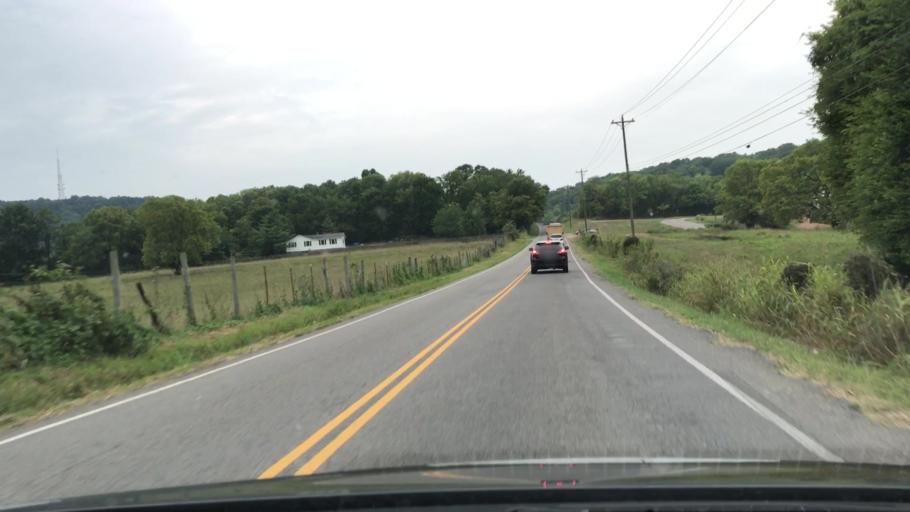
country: US
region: Tennessee
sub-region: Williamson County
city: Nolensville
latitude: 35.9354
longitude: -86.7116
